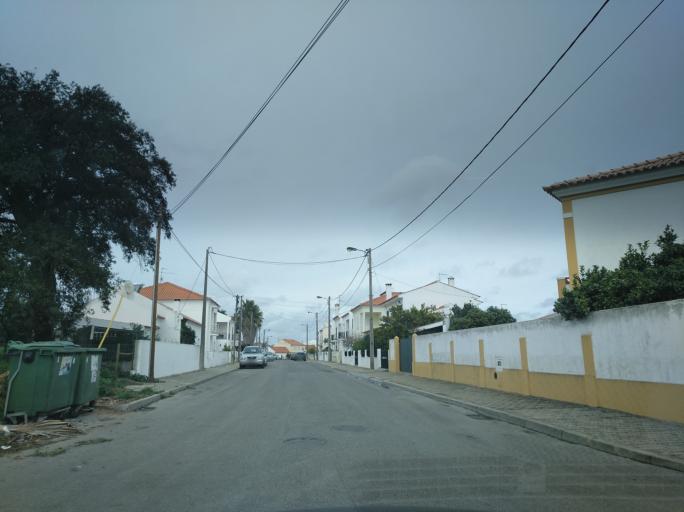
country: PT
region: Setubal
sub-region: Grandola
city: Grandola
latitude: 38.1803
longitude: -8.5723
